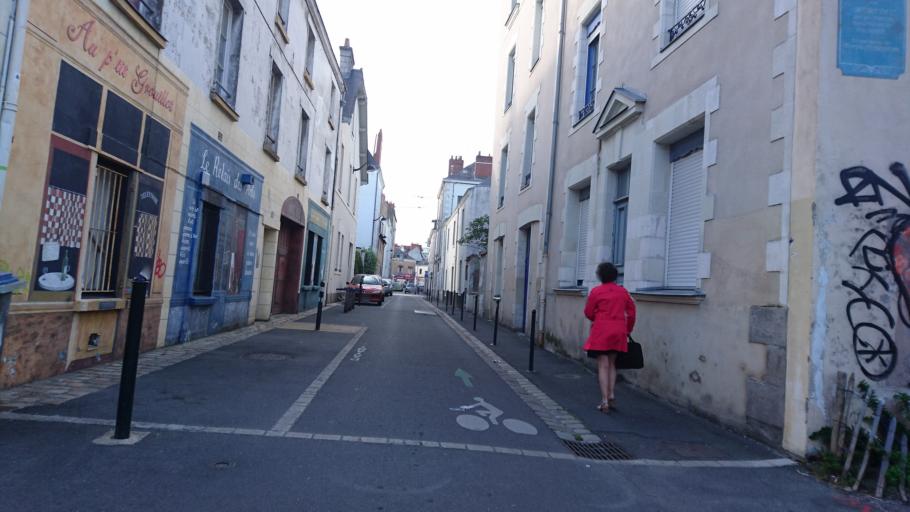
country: FR
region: Pays de la Loire
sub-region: Departement de la Loire-Atlantique
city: Nantes
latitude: 47.2133
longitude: -1.5479
